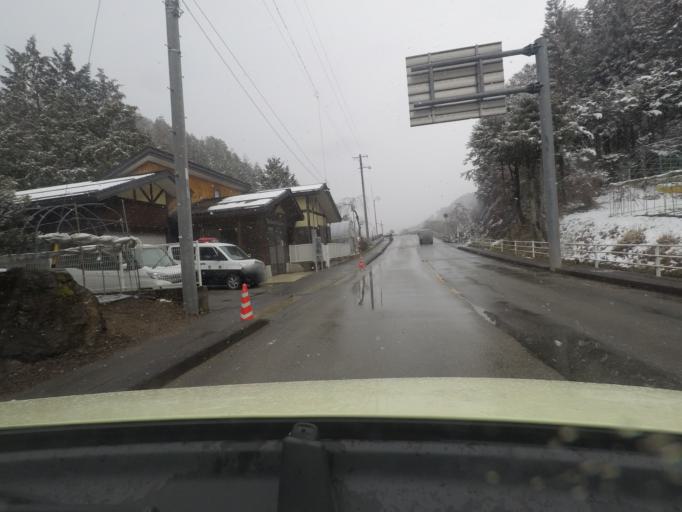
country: JP
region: Gifu
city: Takayama
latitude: 36.1503
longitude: 137.2834
